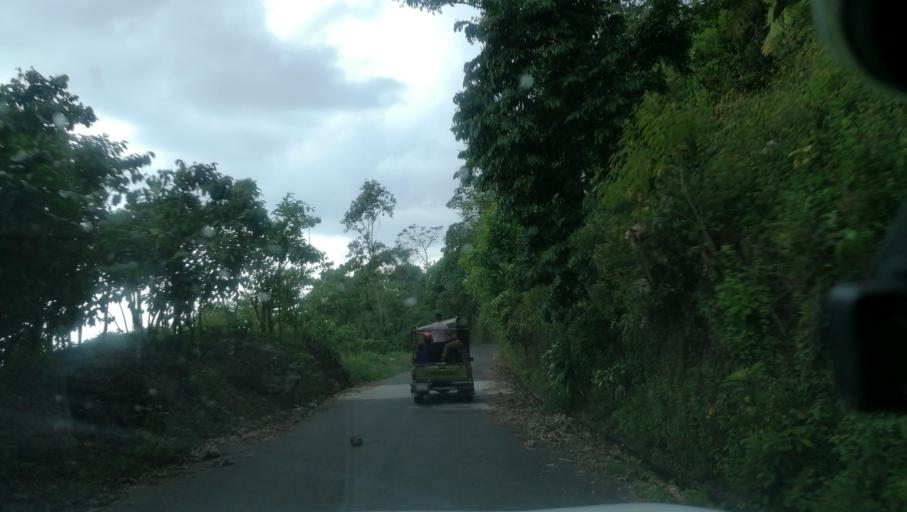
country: MX
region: Chiapas
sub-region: Cacahoatan
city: Benito Juarez
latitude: 15.0704
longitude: -92.1760
